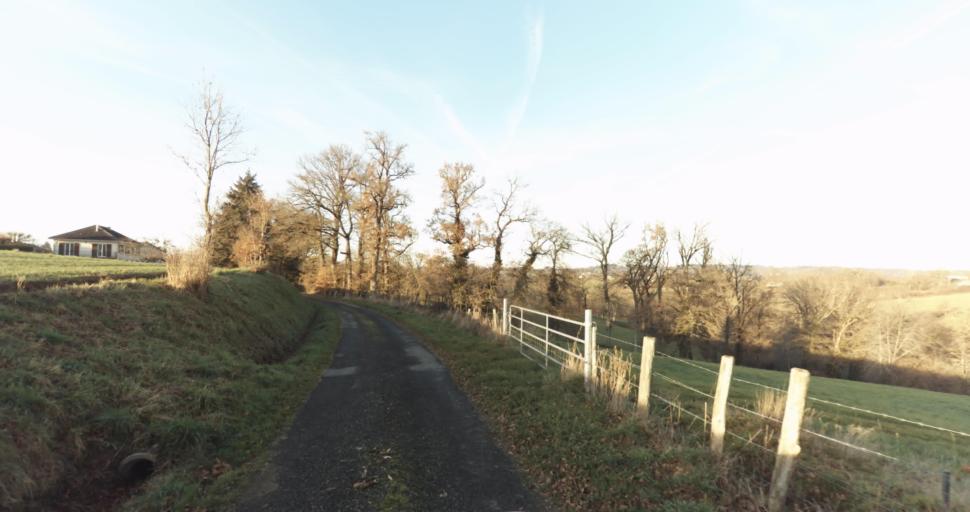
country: FR
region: Limousin
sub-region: Departement de la Haute-Vienne
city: Aixe-sur-Vienne
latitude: 45.7828
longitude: 1.1456
